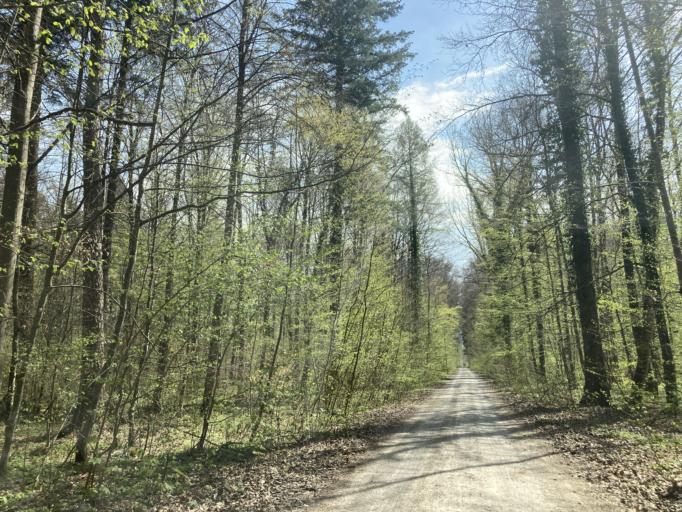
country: DE
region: Baden-Wuerttemberg
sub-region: Tuebingen Region
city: Ofterdingen
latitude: 48.4326
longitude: 8.9937
